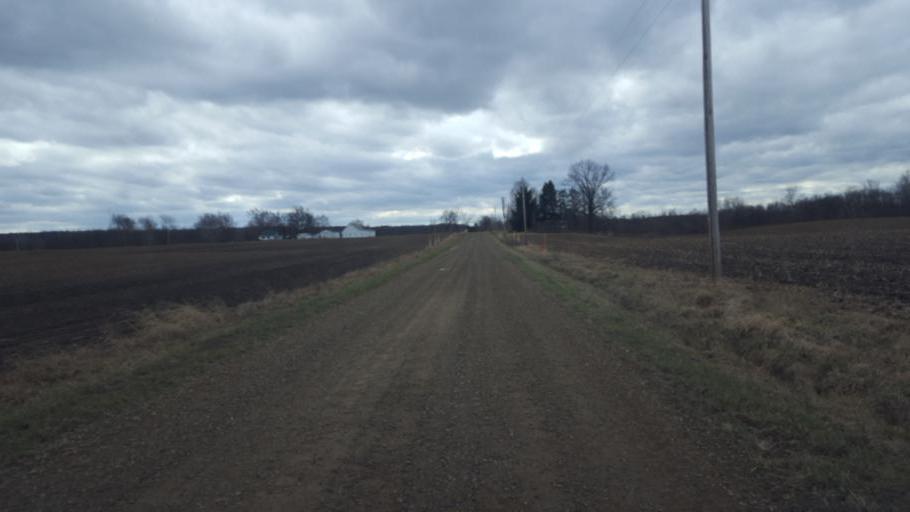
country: US
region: Ohio
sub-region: Licking County
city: Utica
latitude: 40.2715
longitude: -82.4977
